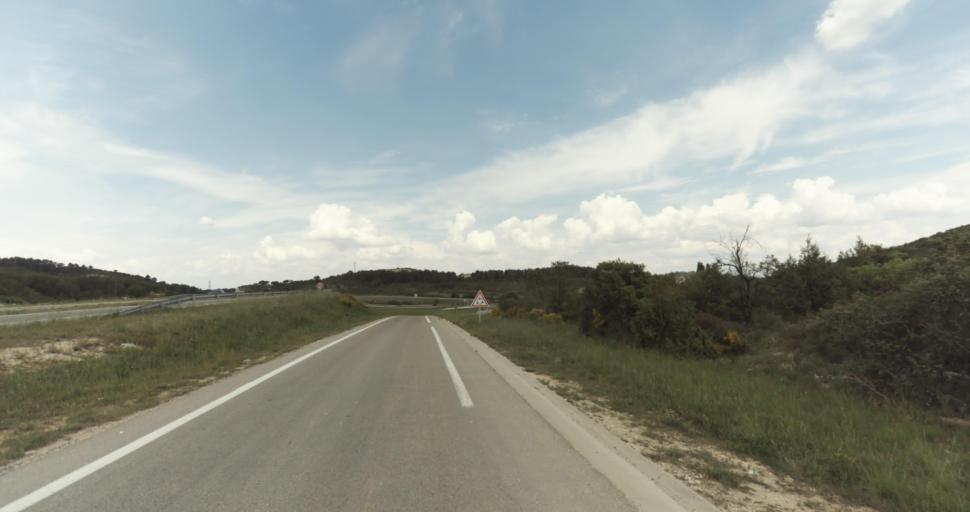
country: FR
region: Languedoc-Roussillon
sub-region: Departement du Gard
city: La Calmette
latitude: 43.9020
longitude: 4.2853
